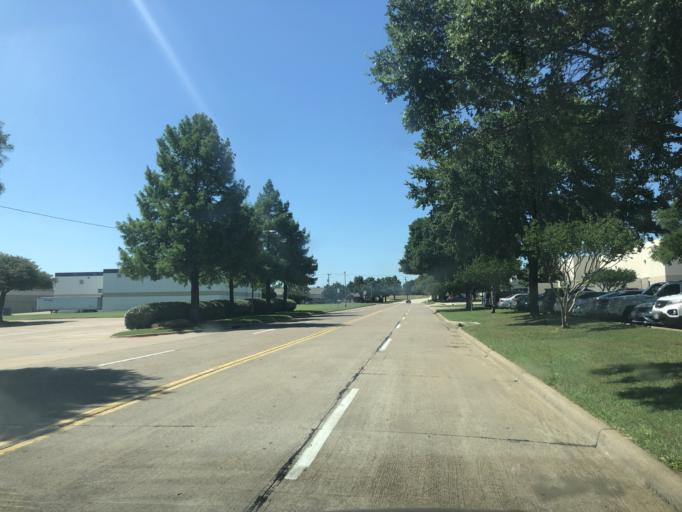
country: US
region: Texas
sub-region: Tarrant County
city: Euless
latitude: 32.7952
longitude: -97.0419
